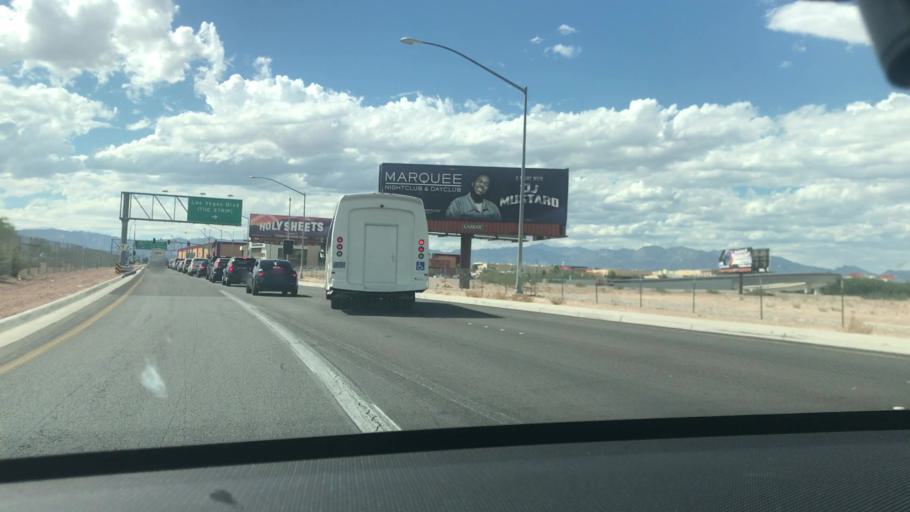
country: US
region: Nevada
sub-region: Clark County
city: Paradise
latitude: 36.0645
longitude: -115.1698
